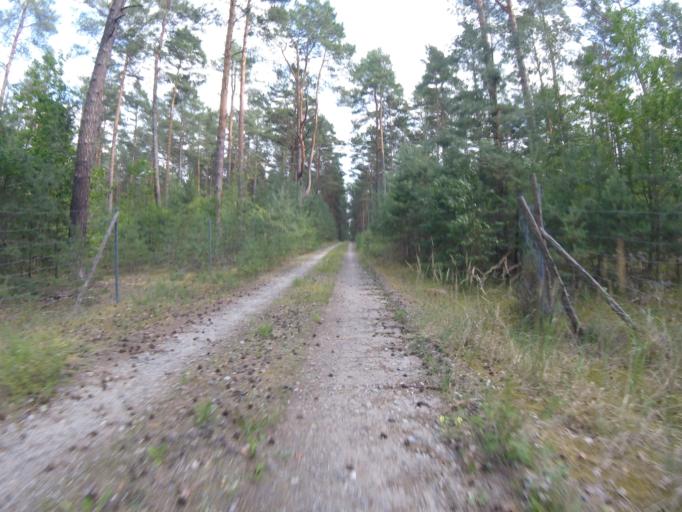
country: DE
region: Brandenburg
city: Halbe
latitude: 52.0611
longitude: 13.7601
